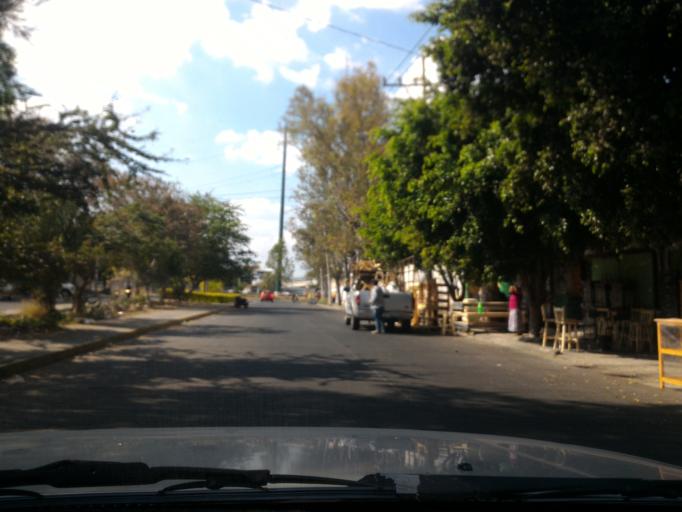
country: MX
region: Jalisco
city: Guadalajara
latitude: 20.6248
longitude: -103.3847
